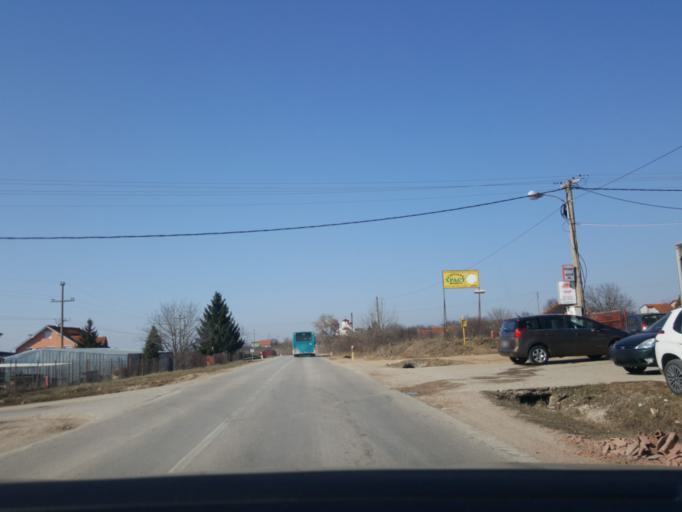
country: RS
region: Central Serbia
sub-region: Nisavski Okrug
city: Nis
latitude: 43.3801
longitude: 21.8227
